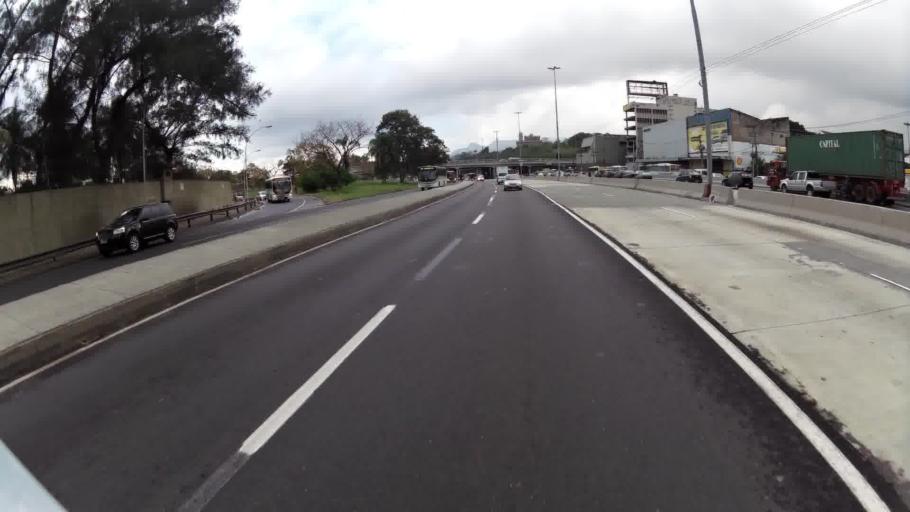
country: BR
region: Rio de Janeiro
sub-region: Rio De Janeiro
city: Rio de Janeiro
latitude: -22.8691
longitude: -43.2471
